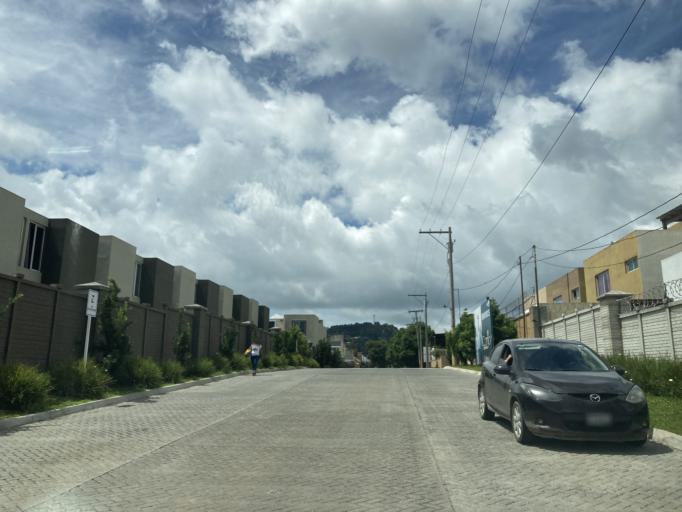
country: GT
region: Guatemala
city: San Jose Pinula
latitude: 14.5377
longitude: -90.4357
